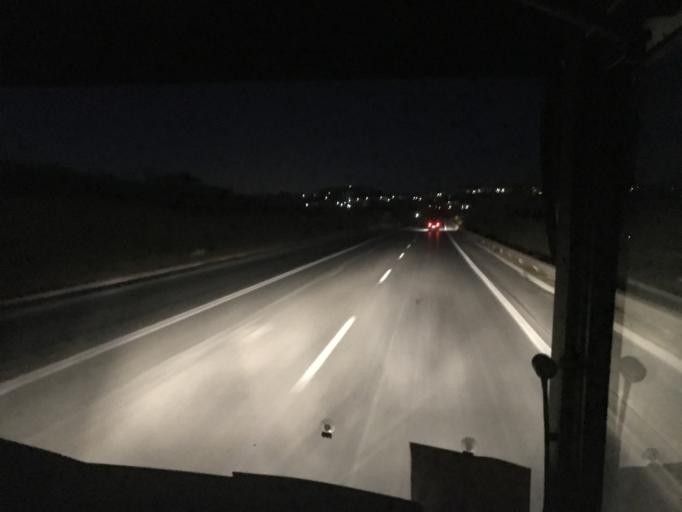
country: GR
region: Crete
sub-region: Nomos Irakleiou
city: Skalanion
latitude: 35.2696
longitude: 25.1849
